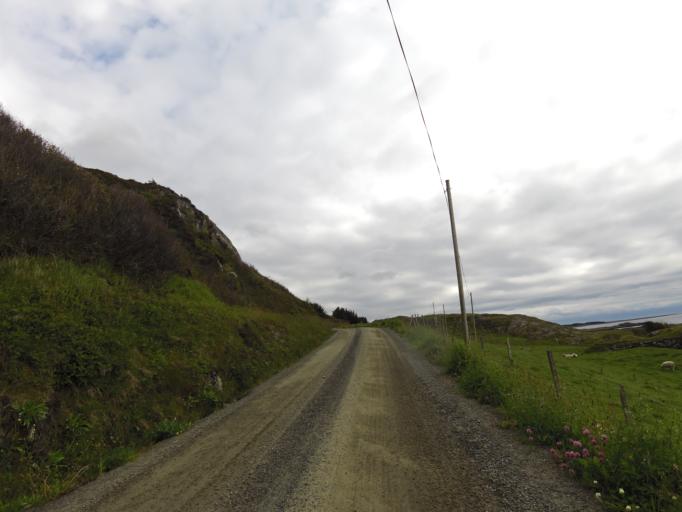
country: NO
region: Vest-Agder
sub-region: Farsund
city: Vestbygd
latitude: 58.1457
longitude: 6.6135
